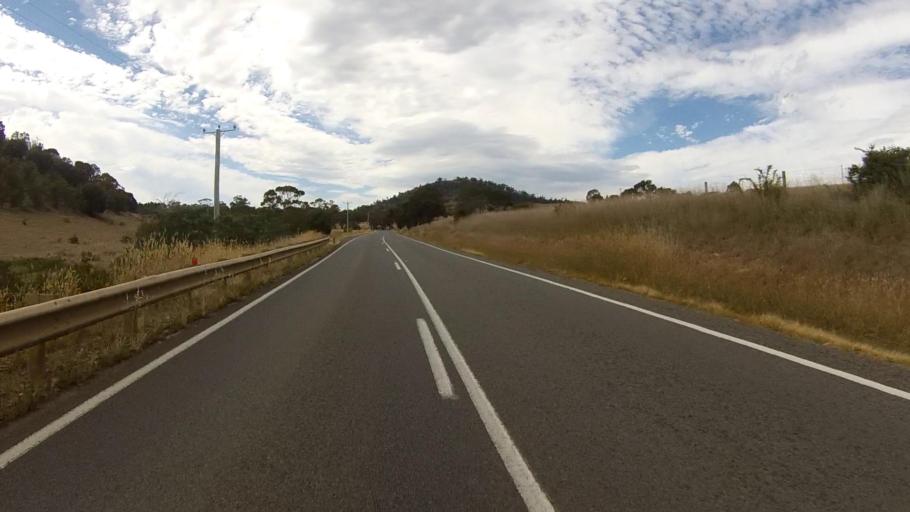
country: AU
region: Tasmania
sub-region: Sorell
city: Sorell
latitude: -42.6977
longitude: 147.4835
